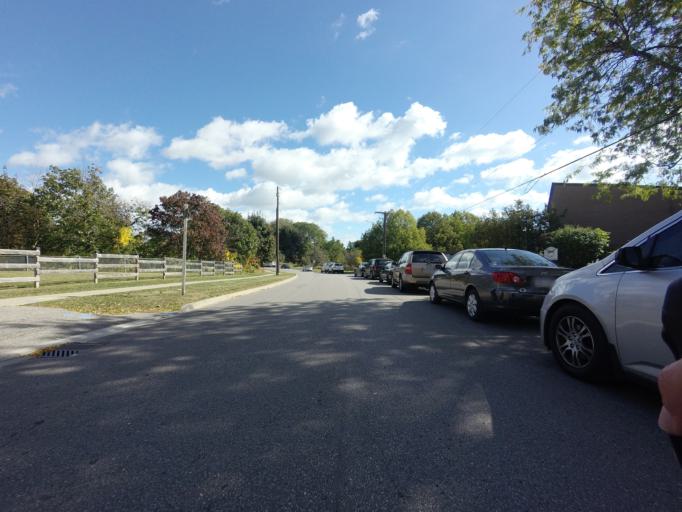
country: CA
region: Ontario
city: Ajax
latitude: 43.8255
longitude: -79.0893
